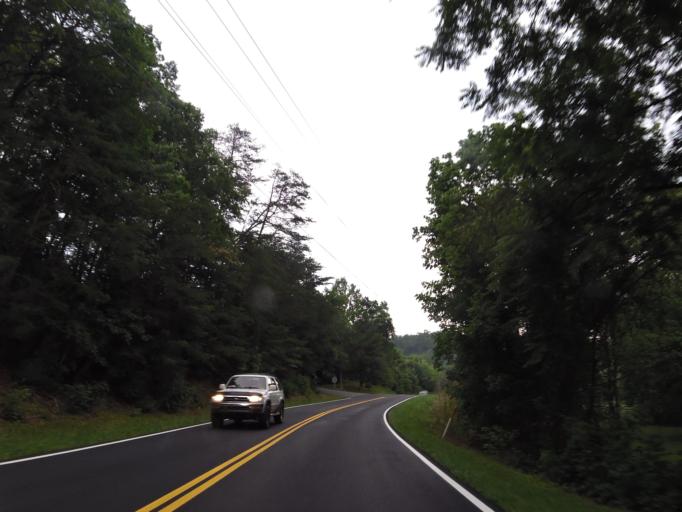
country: US
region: Tennessee
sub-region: Sevier County
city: Pigeon Forge
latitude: 35.8101
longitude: -83.6217
